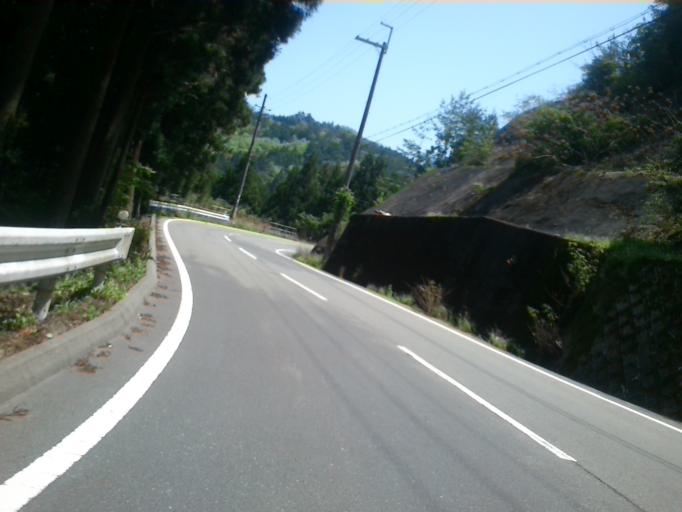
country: JP
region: Kyoto
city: Kameoka
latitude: 34.9244
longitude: 135.5591
